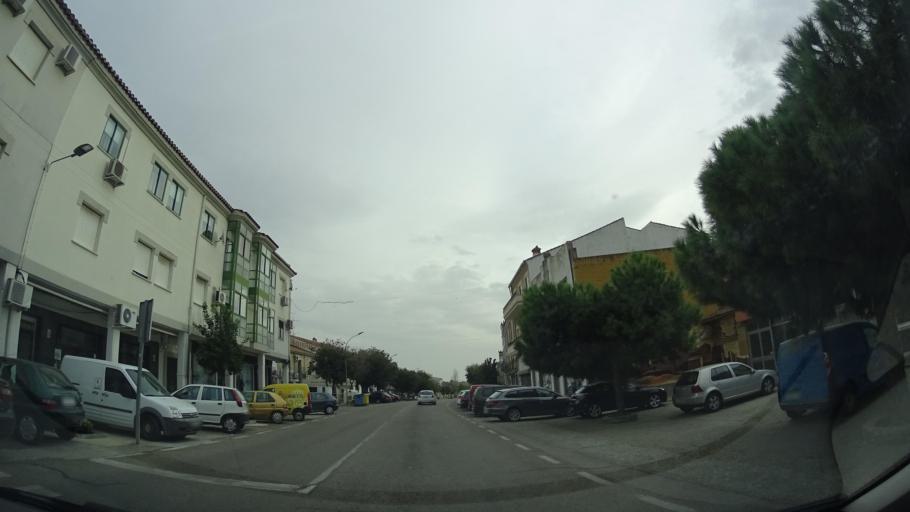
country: ES
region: Extremadura
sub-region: Provincia de Caceres
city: Trujillo
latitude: 39.4562
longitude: -5.8814
